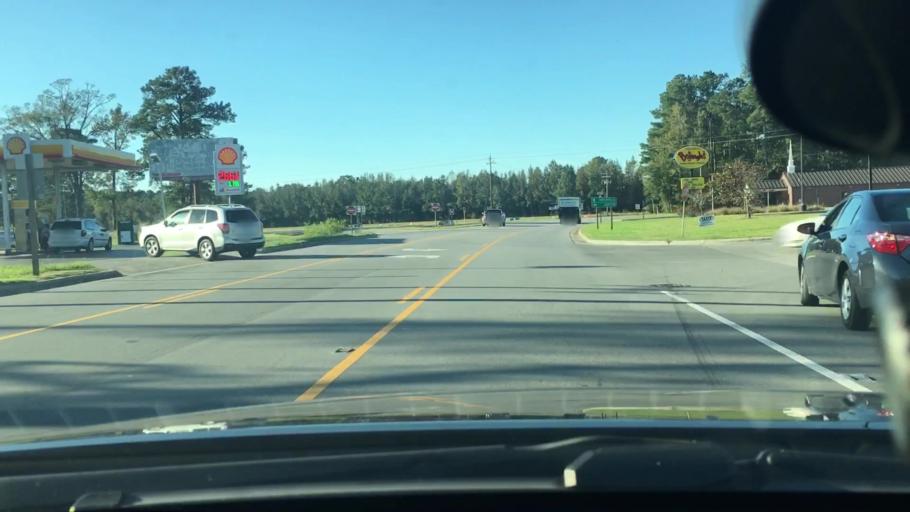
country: US
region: North Carolina
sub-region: Craven County
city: Vanceboro
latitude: 35.3115
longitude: -77.1605
